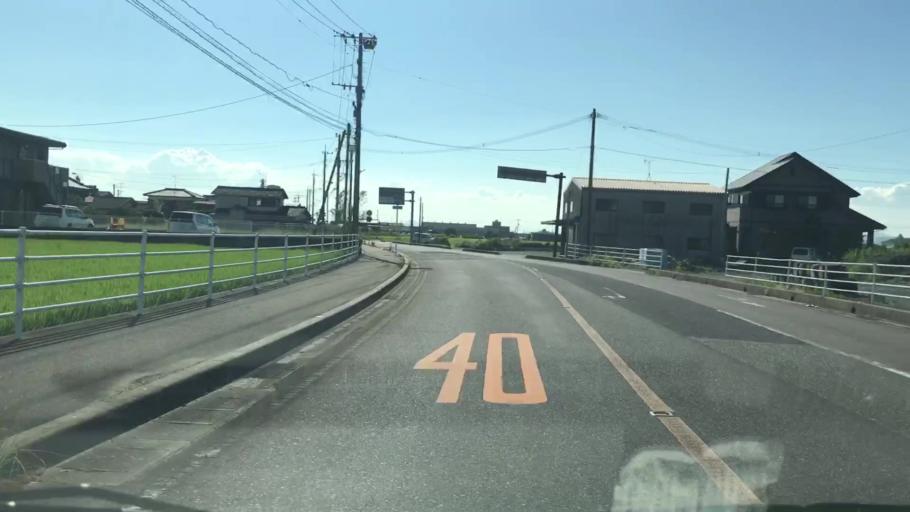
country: JP
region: Saga Prefecture
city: Okawa
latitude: 33.1905
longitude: 130.3312
